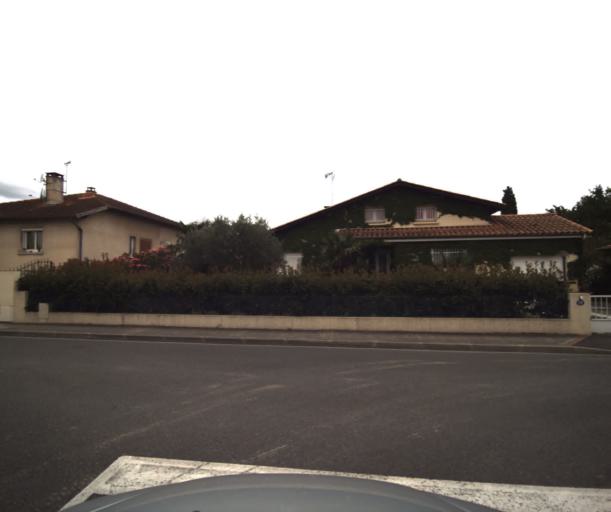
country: FR
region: Midi-Pyrenees
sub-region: Departement de la Haute-Garonne
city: Muret
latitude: 43.4672
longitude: 1.3384
